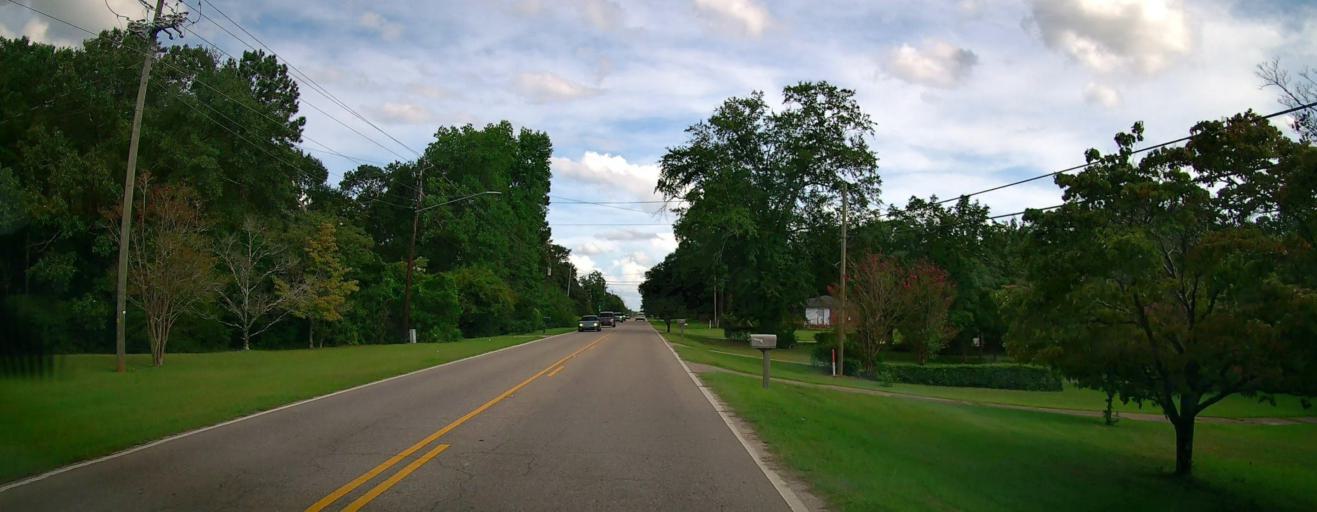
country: US
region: Alabama
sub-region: Russell County
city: Phenix City
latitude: 32.5186
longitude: -85.0273
